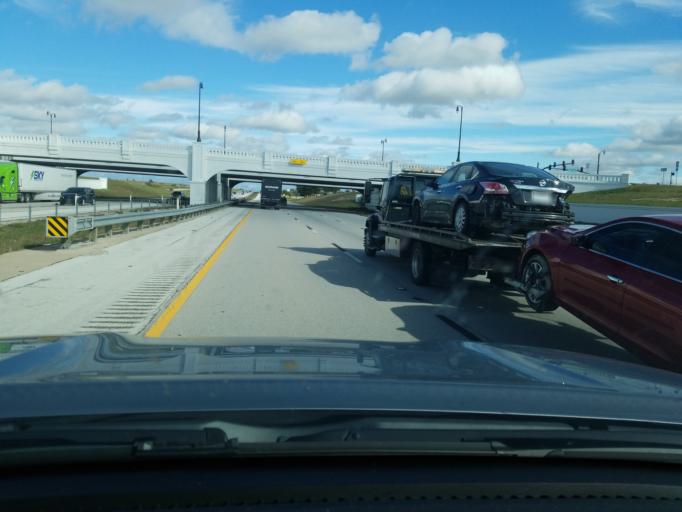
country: US
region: Texas
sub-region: Parker County
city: Aledo
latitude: 32.7209
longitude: -97.5587
